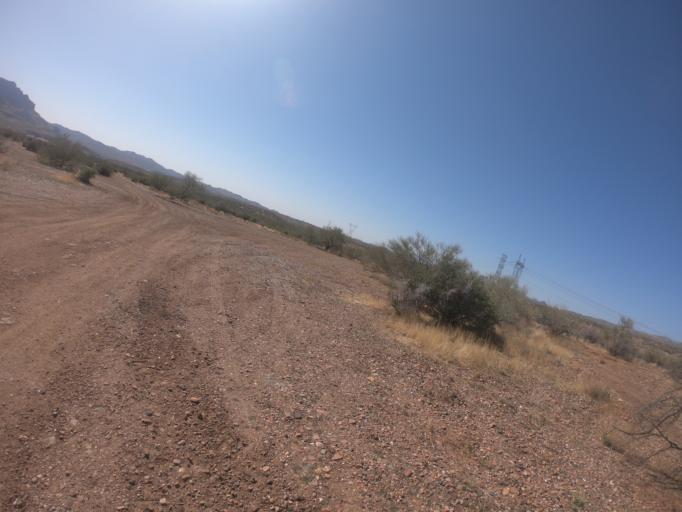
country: US
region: Arizona
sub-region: Pinal County
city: Superior
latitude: 33.2969
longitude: -111.1263
